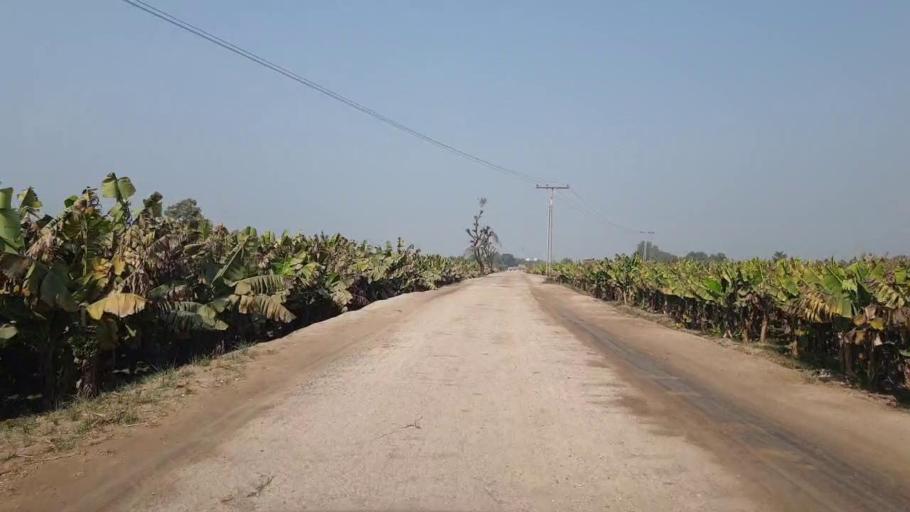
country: PK
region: Sindh
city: Bhit Shah
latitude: 25.7948
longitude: 68.4979
